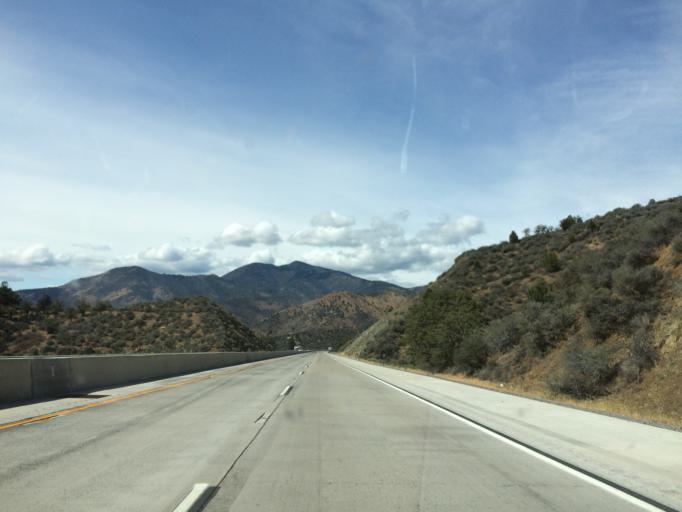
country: US
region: California
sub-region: Siskiyou County
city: Montague
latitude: 41.8140
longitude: -122.5733
